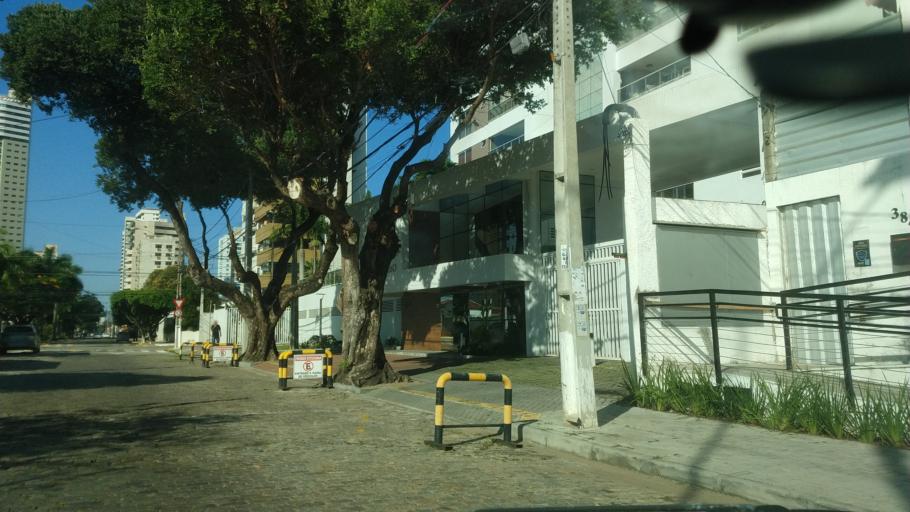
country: BR
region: Rio Grande do Norte
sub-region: Natal
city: Natal
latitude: -5.7840
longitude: -35.1985
